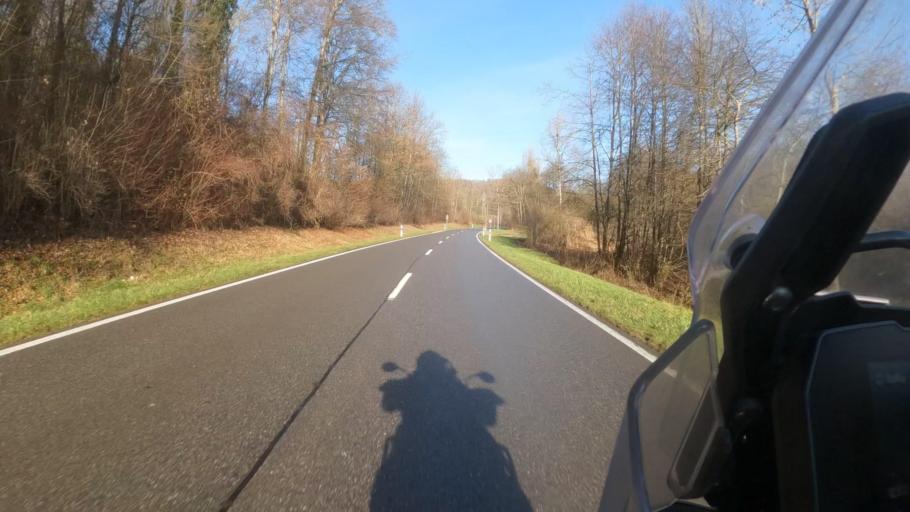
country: DE
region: Baden-Wuerttemberg
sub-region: Freiburg Region
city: Neuhausen
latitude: 47.8141
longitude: 8.7341
